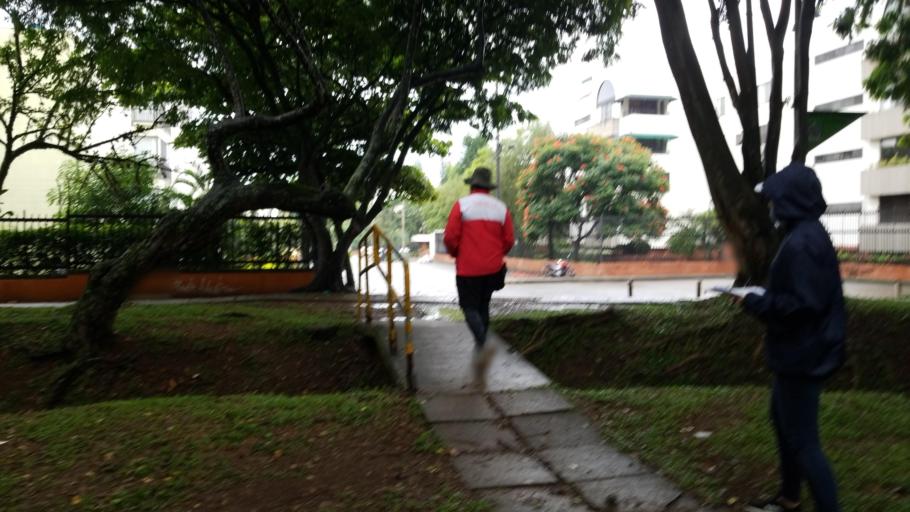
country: CO
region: Valle del Cauca
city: Cali
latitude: 3.3773
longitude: -76.5407
